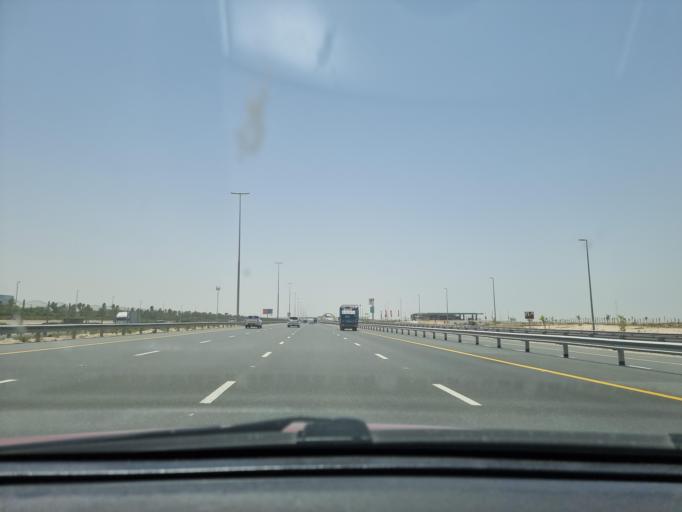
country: AE
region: Dubai
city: Dubai
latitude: 24.9284
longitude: 55.0045
